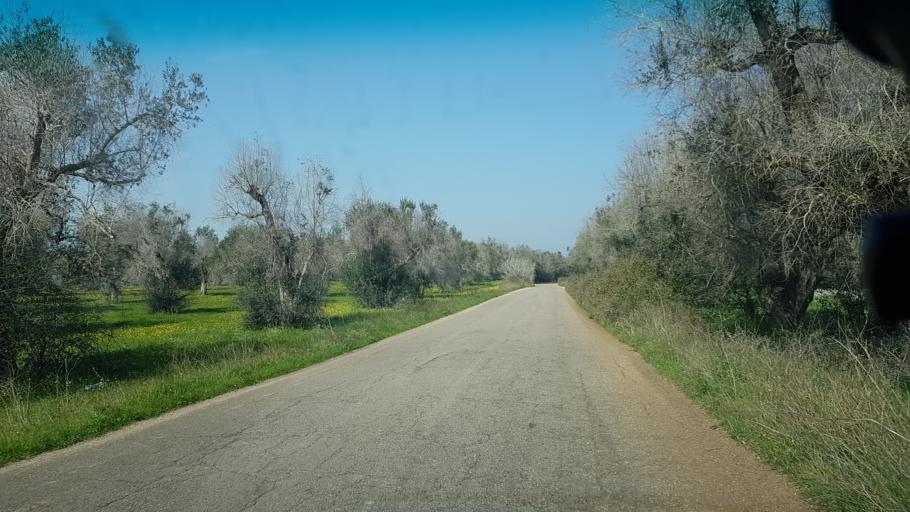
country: IT
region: Apulia
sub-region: Provincia di Brindisi
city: Torchiarolo
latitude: 40.4826
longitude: 18.0305
